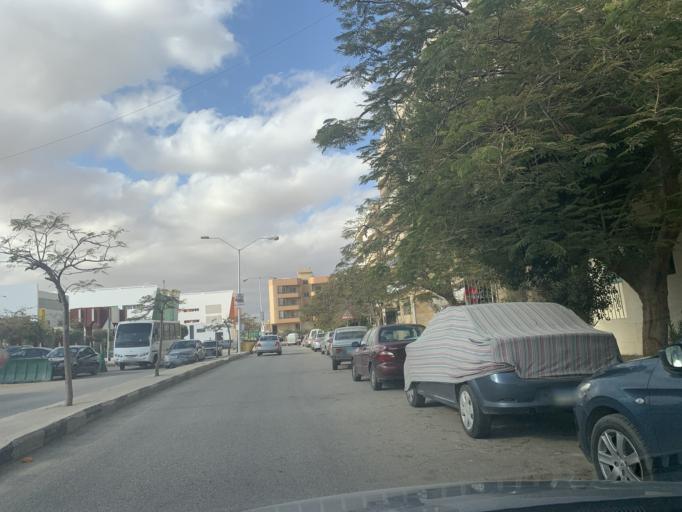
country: EG
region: Al Jizah
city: Madinat Sittah Uktubar
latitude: 29.9847
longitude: 30.9374
